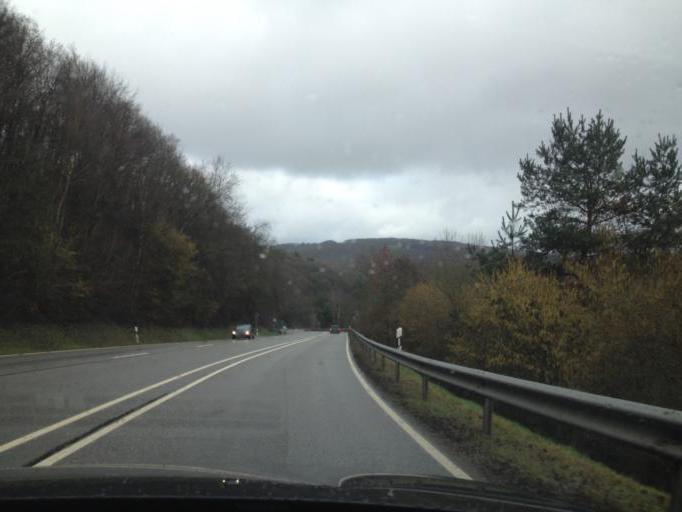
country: DE
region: Rheinland-Pfalz
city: Oberbrombach
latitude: 49.7053
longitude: 7.2608
